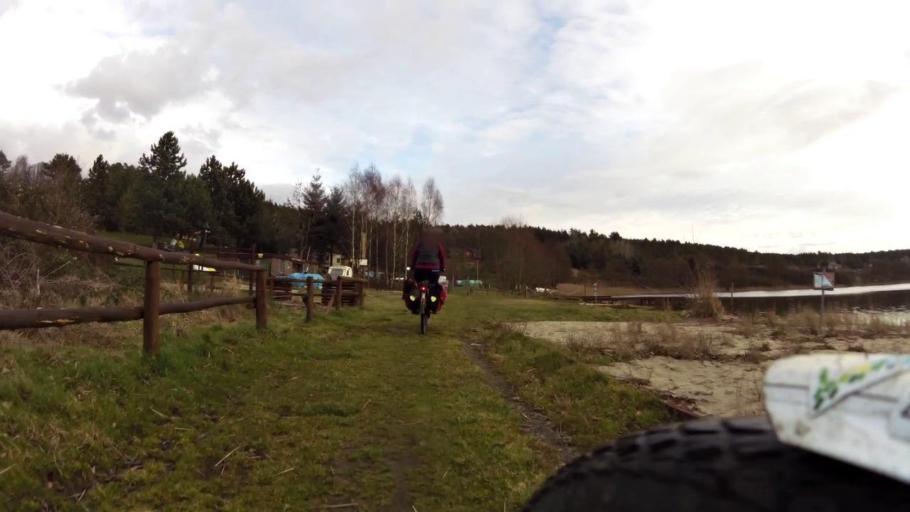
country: PL
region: West Pomeranian Voivodeship
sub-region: Powiat kamienski
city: Wolin
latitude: 53.9628
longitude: 14.5744
